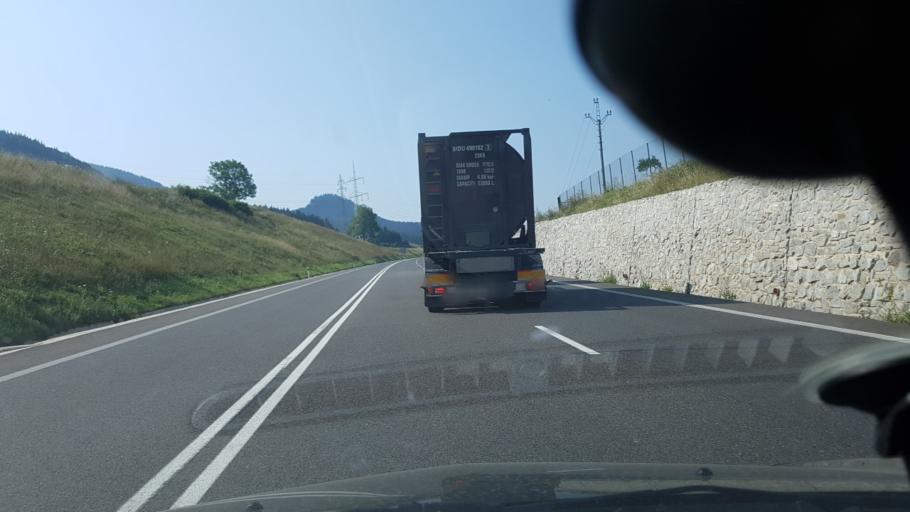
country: SK
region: Zilinsky
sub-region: Okres Dolny Kubin
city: Dolny Kubin
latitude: 49.1741
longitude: 19.2999
